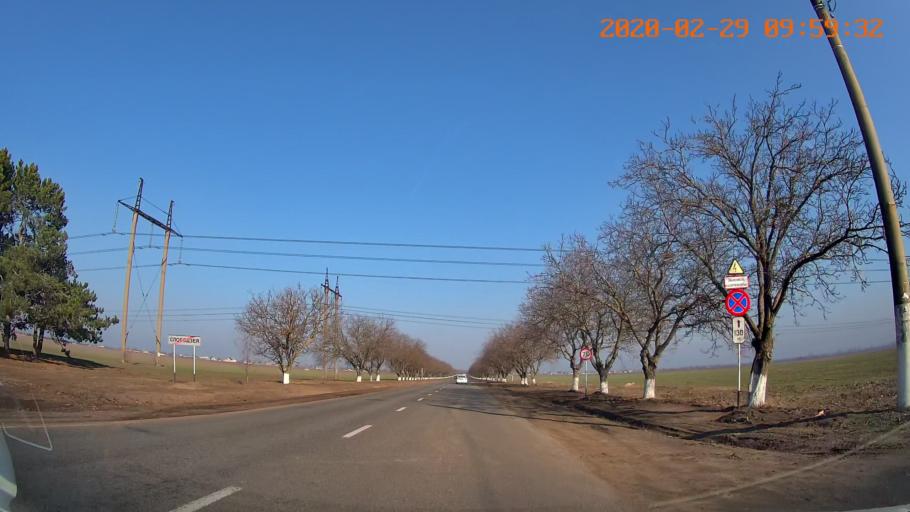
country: MD
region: Telenesti
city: Slobozia
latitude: 46.7579
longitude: 29.6882
